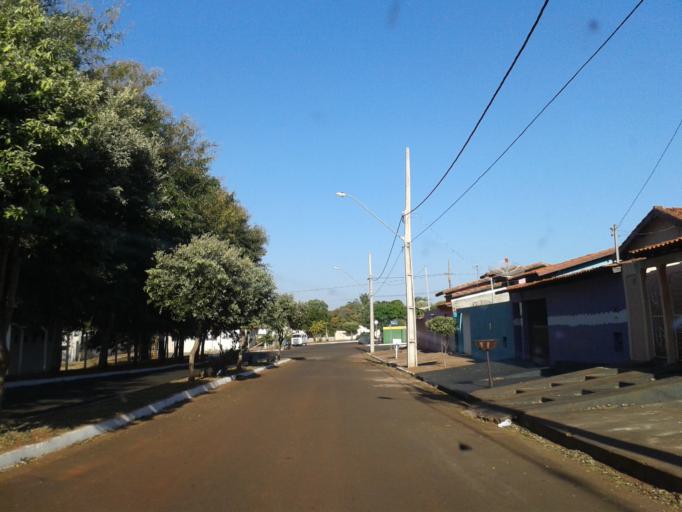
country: BR
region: Minas Gerais
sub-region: Santa Vitoria
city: Santa Vitoria
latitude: -18.8320
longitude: -50.1370
